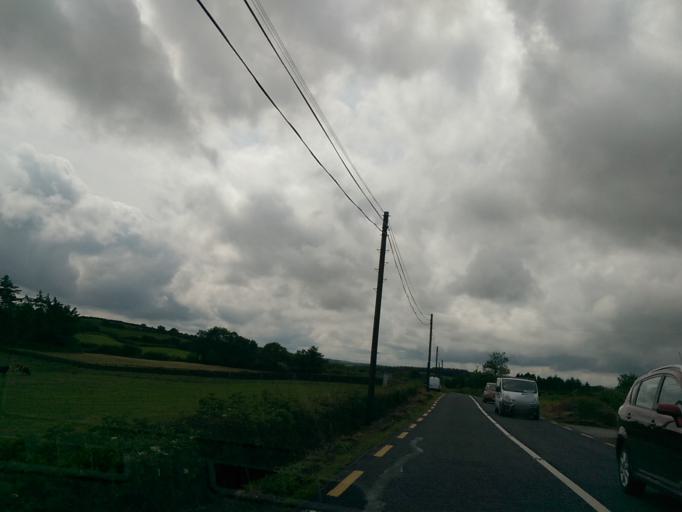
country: IE
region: Munster
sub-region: An Clar
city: Ennis
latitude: 52.7726
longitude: -9.0891
